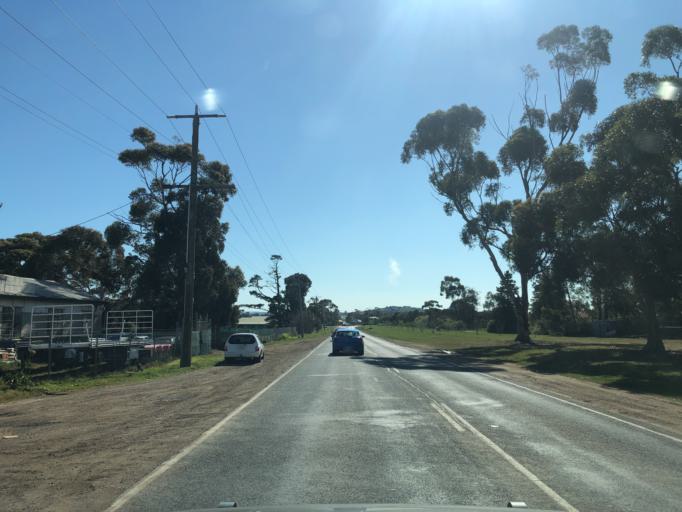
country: AU
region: Victoria
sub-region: Hume
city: Diggers Rest
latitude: -37.6311
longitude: 144.7234
